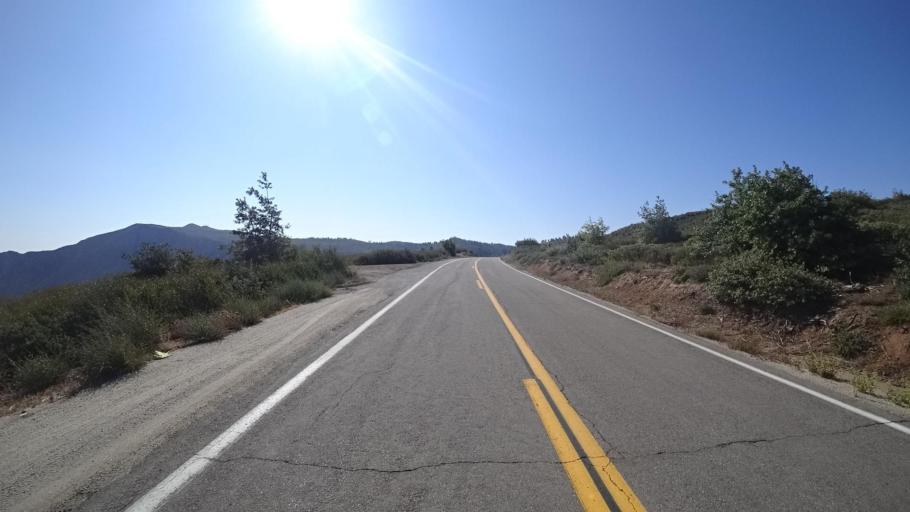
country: US
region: California
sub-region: San Diego County
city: Pine Valley
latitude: 32.9032
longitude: -116.4557
